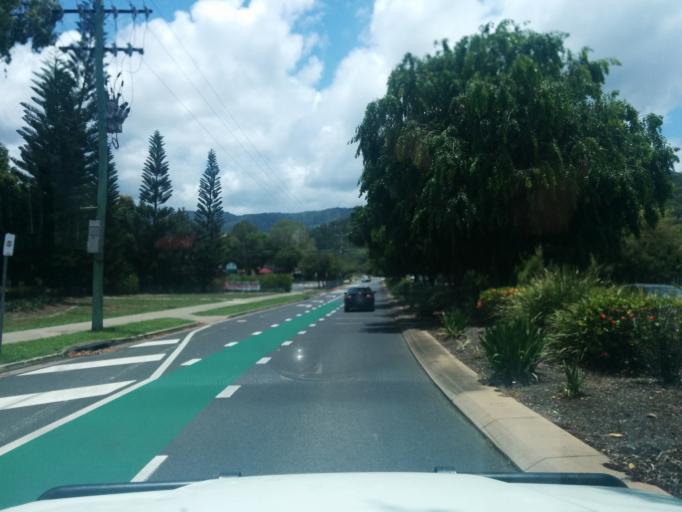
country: AU
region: Queensland
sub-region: Cairns
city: Trinity Beach
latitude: -16.8094
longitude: 145.6962
